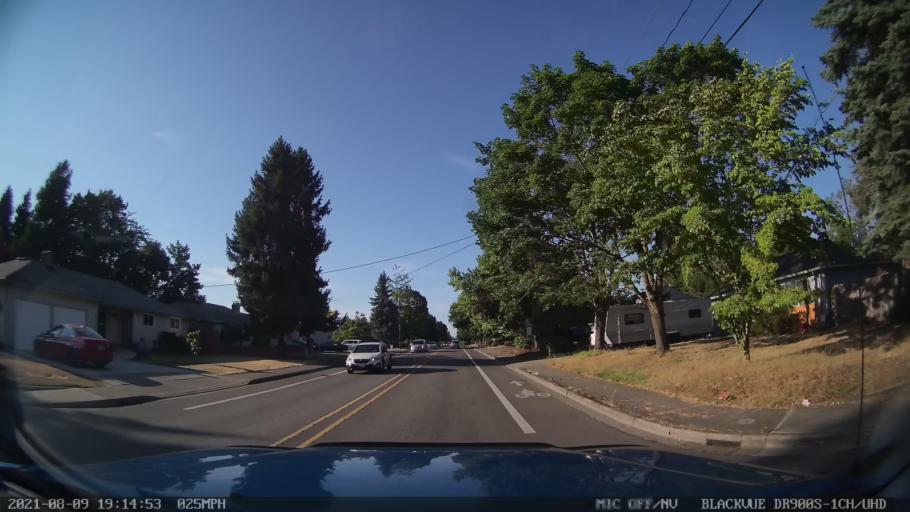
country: US
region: Oregon
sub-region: Marion County
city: Four Corners
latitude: 44.9360
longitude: -122.9917
